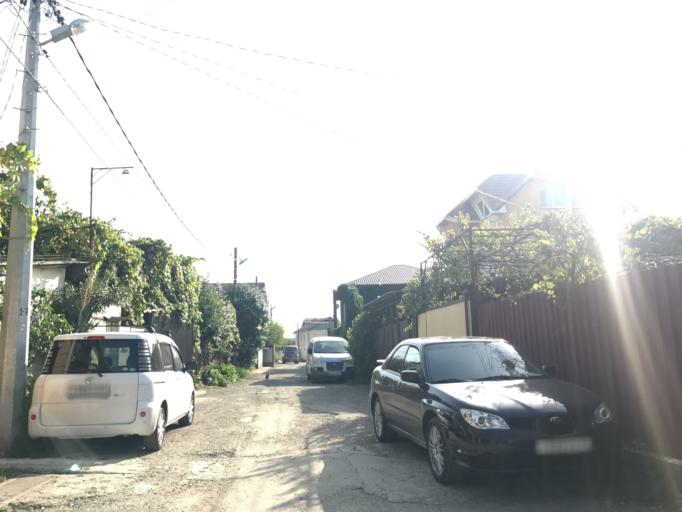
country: RU
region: Krasnodarskiy
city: Adler
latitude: 43.4202
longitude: 39.9400
